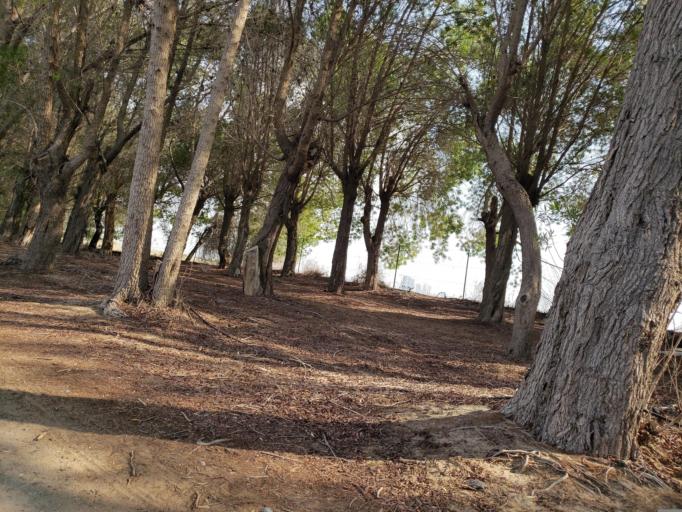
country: AE
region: Dubai
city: Dubai
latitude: 25.1370
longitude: 55.3415
